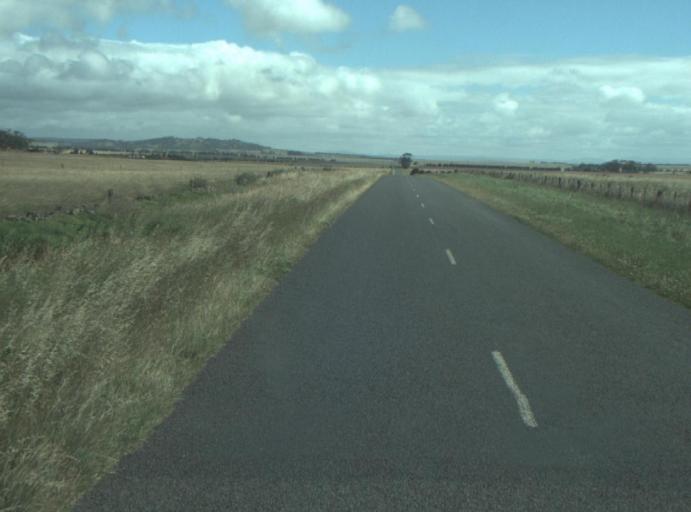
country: AU
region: Victoria
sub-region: Greater Geelong
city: Lara
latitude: -37.9396
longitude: 144.3100
